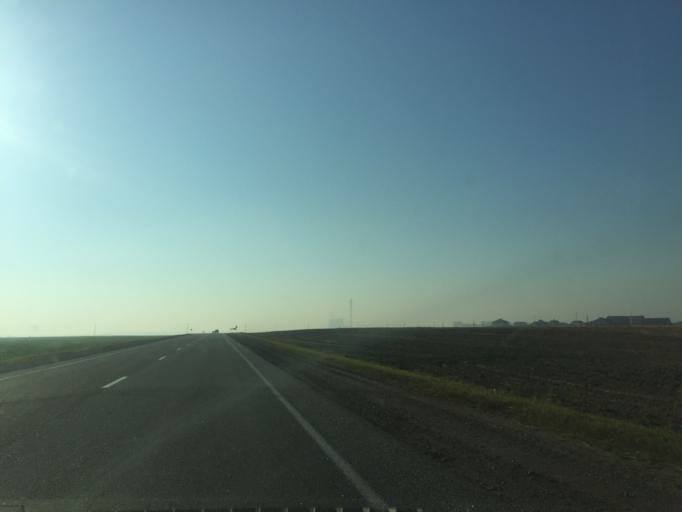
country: BY
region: Gomel
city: Kastsyukowka
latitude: 52.4821
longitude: 30.8205
